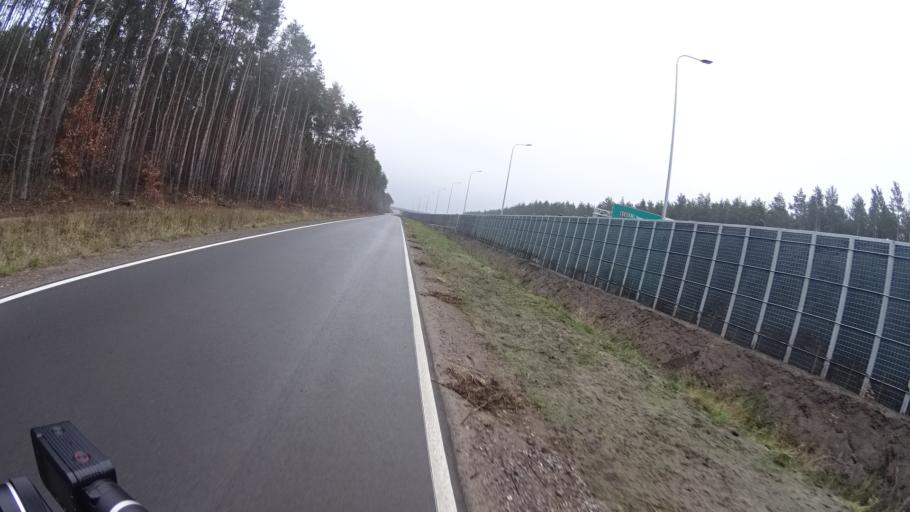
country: PL
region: Masovian Voivodeship
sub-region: Warszawa
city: Wawer
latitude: 52.1666
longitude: 21.1885
